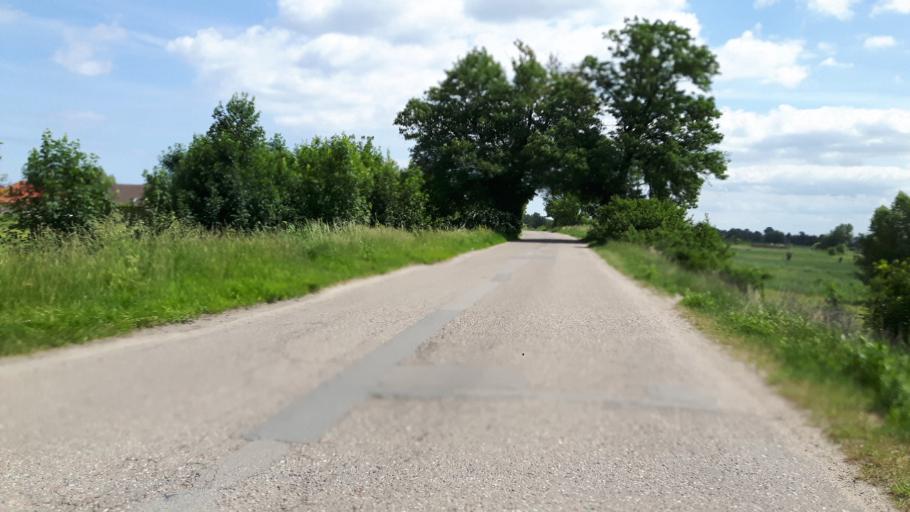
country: PL
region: Pomeranian Voivodeship
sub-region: Powiat gdanski
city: Cedry Wielkie
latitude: 54.3353
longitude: 18.8134
